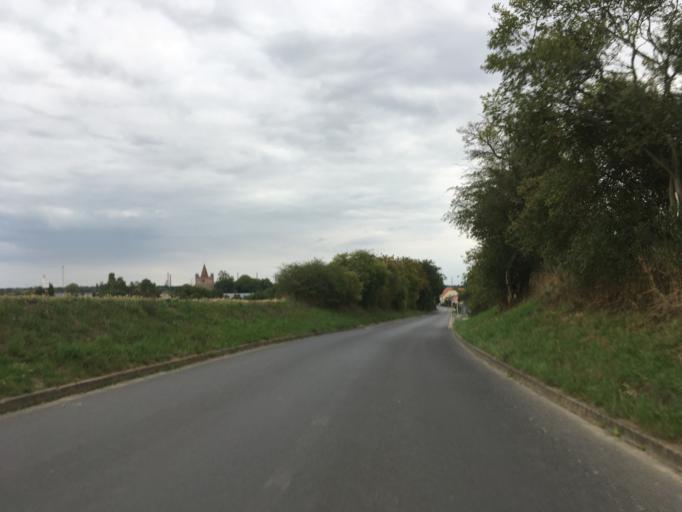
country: DE
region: Brandenburg
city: Meyenburg
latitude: 53.0866
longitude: 14.1948
